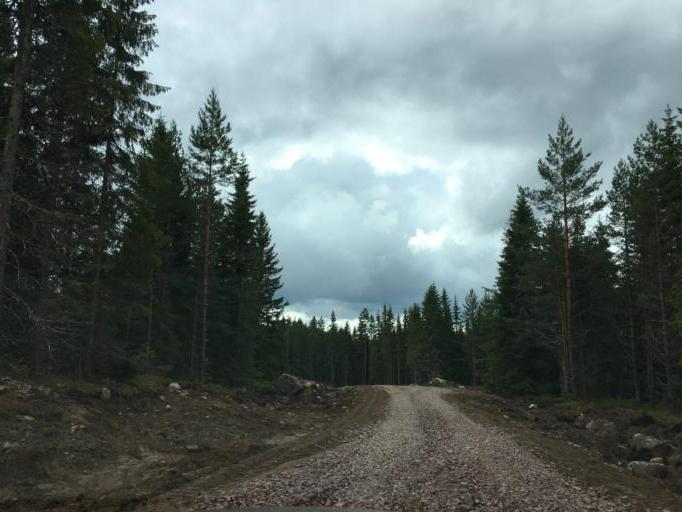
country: SE
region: Vaermland
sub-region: Filipstads Kommun
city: Lesjofors
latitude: 60.0853
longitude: 14.4673
